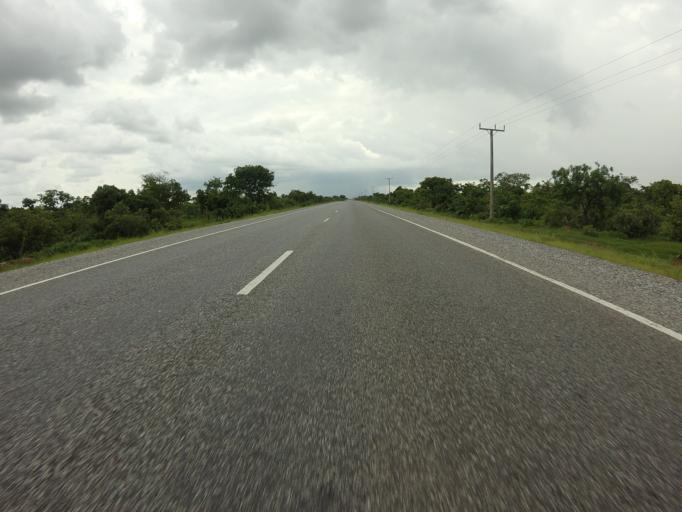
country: GH
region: Northern
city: Tamale
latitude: 9.1287
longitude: -1.2949
